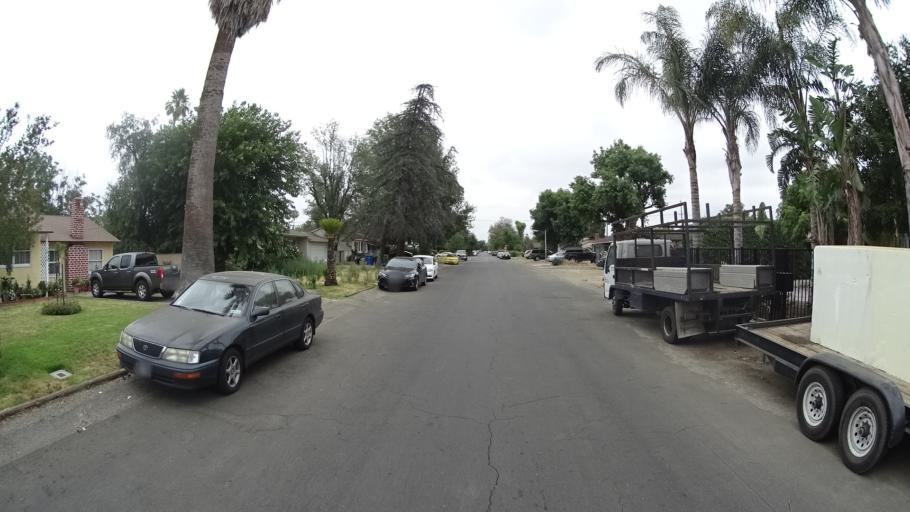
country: US
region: California
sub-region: Los Angeles County
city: San Fernando
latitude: 34.2403
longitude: -118.4551
